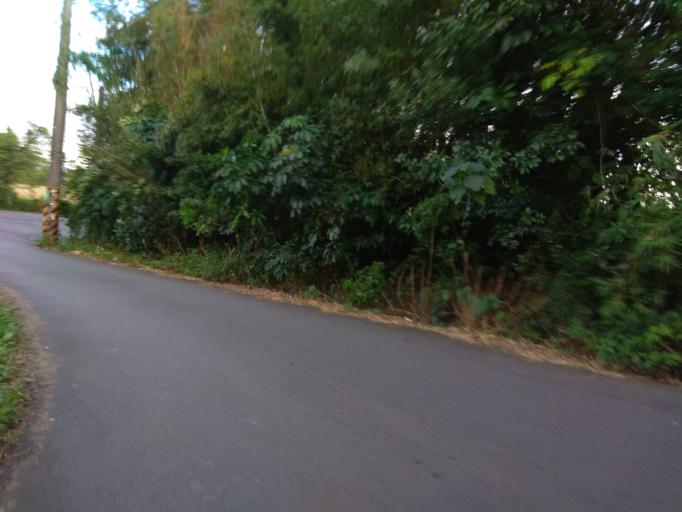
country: TW
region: Taiwan
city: Daxi
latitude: 24.9289
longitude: 121.1892
